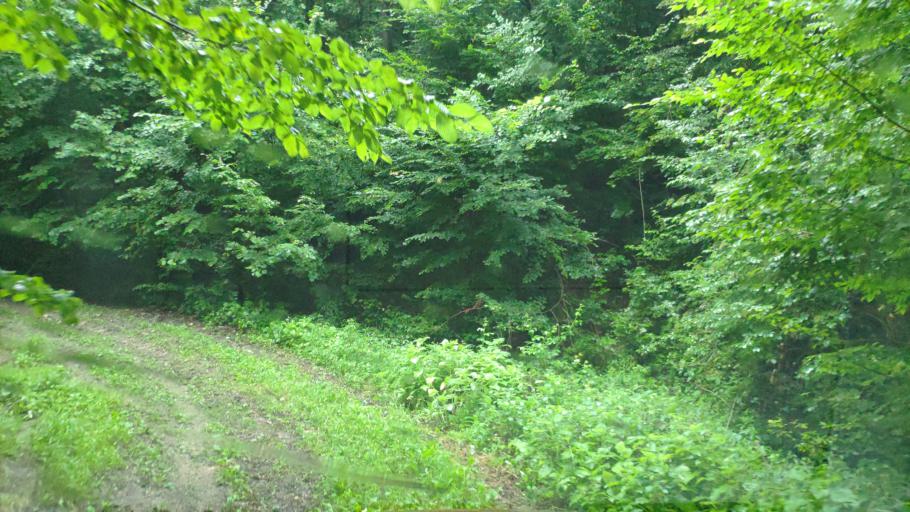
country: SK
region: Presovsky
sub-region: Okres Presov
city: Presov
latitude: 48.8679
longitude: 21.1967
